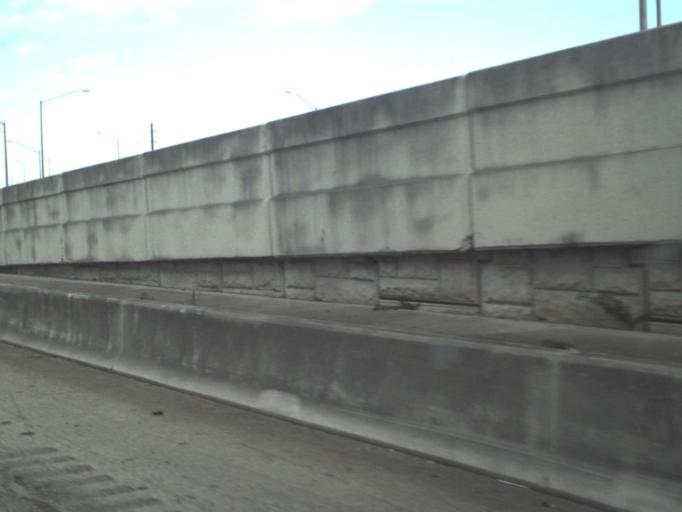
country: US
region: Florida
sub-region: Palm Beach County
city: West Palm Beach
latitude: 26.6832
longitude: -80.0692
